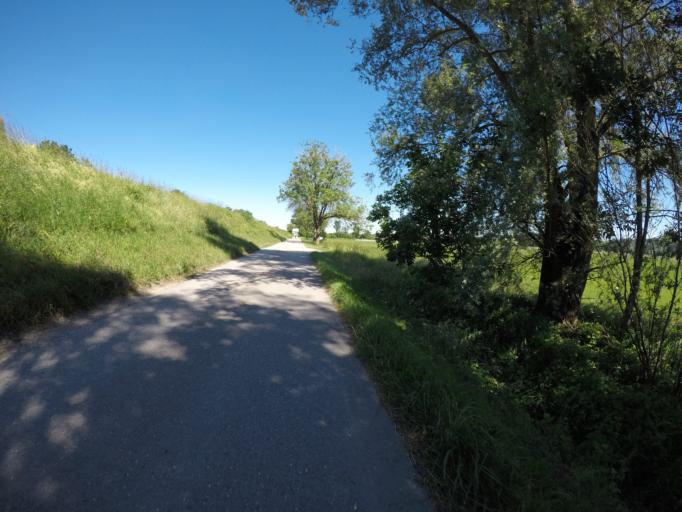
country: DE
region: Bavaria
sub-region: Upper Bavaria
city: Haag an der Amper
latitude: 48.4544
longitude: 11.8198
